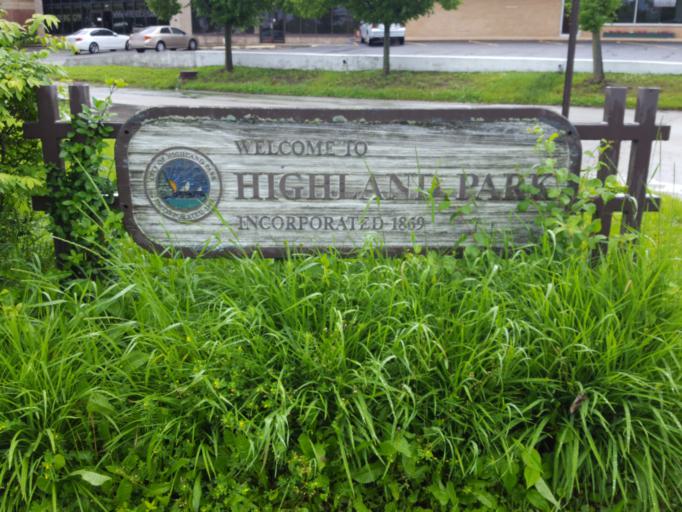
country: US
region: Illinois
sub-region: Lake County
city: Highwood
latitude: 42.2180
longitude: -87.8217
